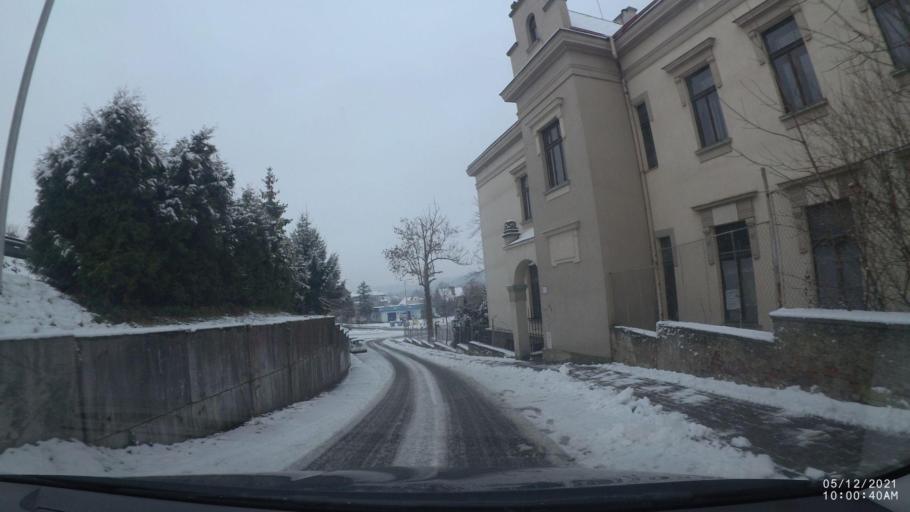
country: CZ
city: Kostelec nad Orlici
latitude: 50.1230
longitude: 16.2080
